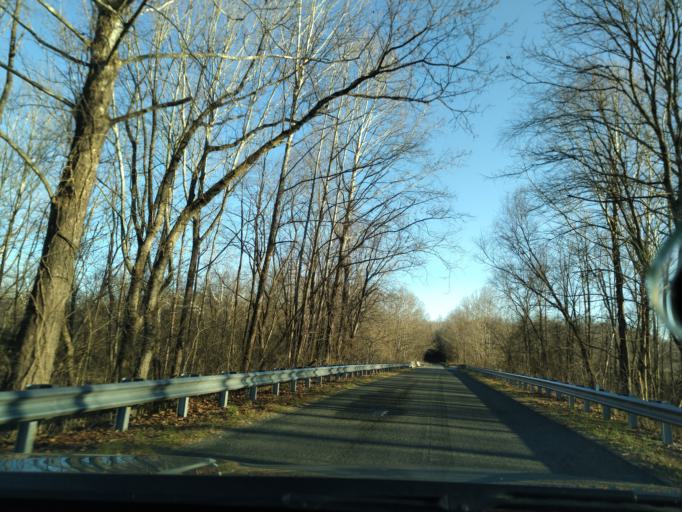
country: US
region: Virginia
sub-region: Prince Edward County
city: Hampden Sydney
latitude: 37.3529
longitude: -78.6007
